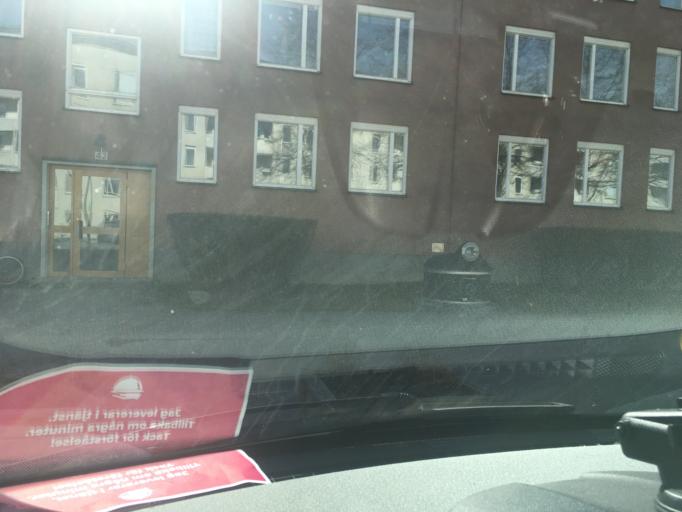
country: SE
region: Stockholm
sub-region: Stockholms Kommun
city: Arsta
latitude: 59.3081
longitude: 18.0192
